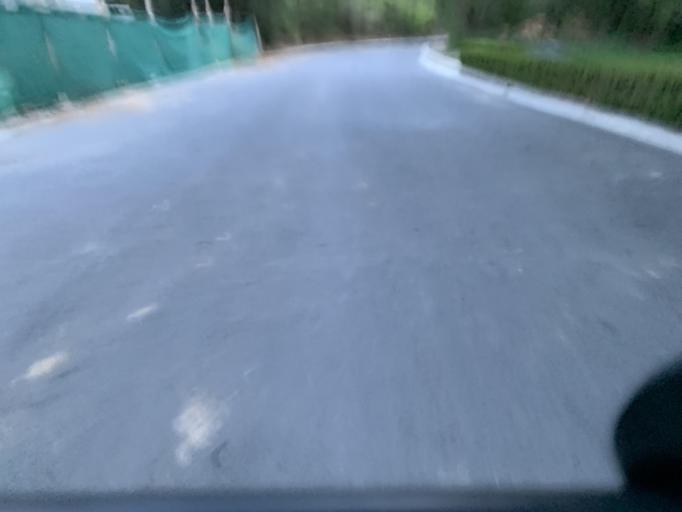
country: MX
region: Nuevo Leon
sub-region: Juarez
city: Bosques de San Pedro
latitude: 25.5212
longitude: -100.1893
